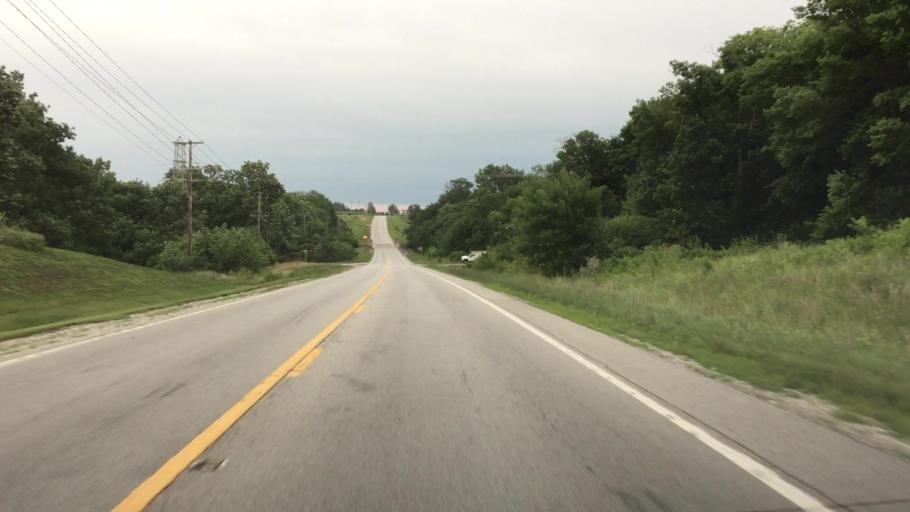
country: US
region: Iowa
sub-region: Lee County
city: Keokuk
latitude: 40.3609
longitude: -91.3632
